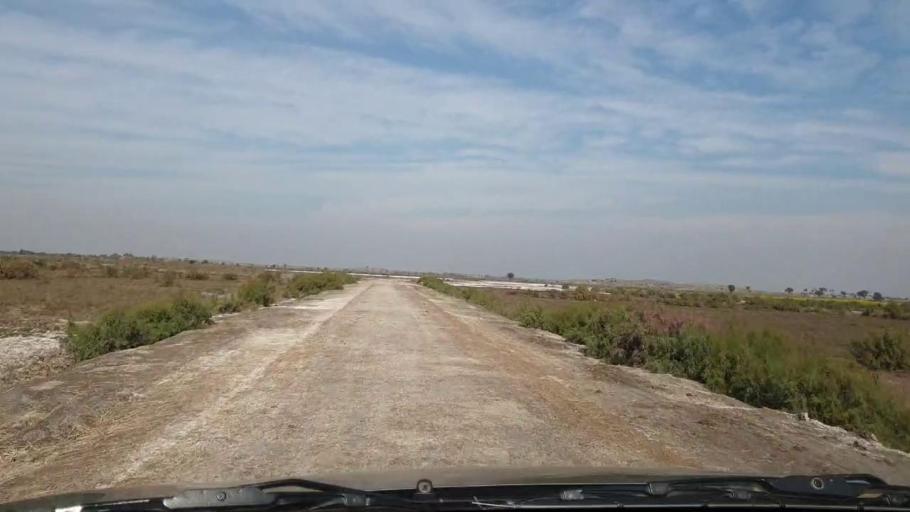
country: PK
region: Sindh
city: Jam Sahib
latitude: 26.2747
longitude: 68.7047
